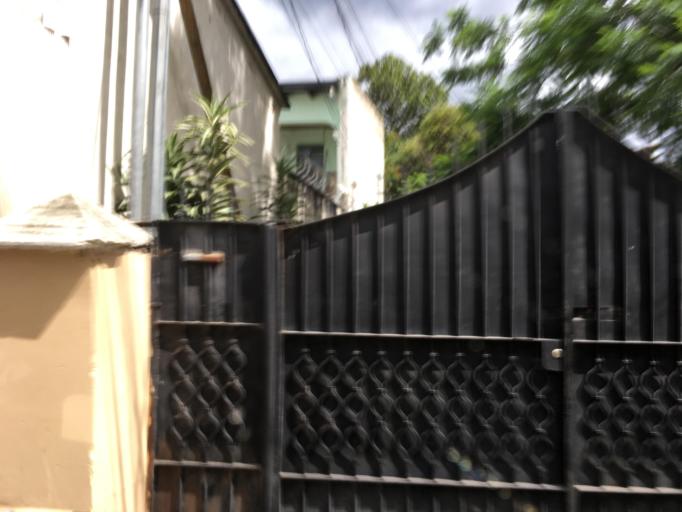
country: GT
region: Sacatepequez
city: Antigua Guatemala
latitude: 14.5526
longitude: -90.7416
